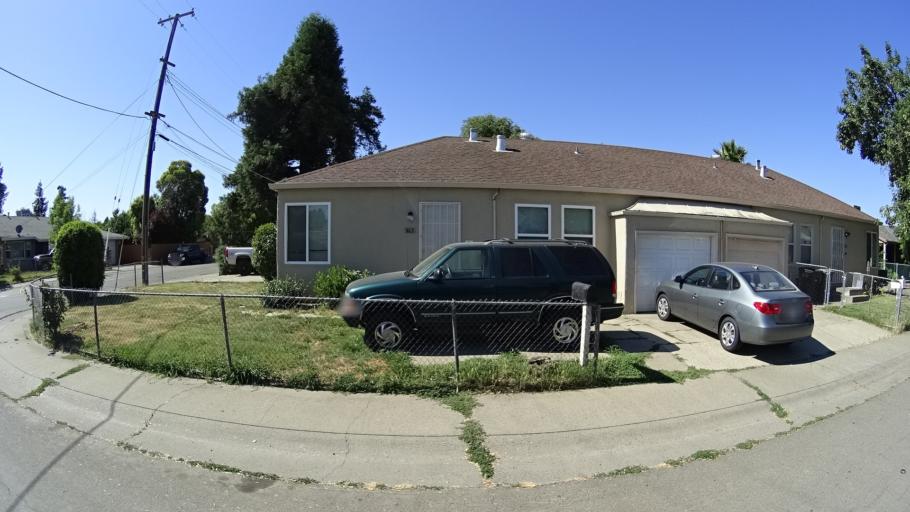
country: US
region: California
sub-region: Sacramento County
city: Parkway
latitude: 38.5287
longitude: -121.4775
